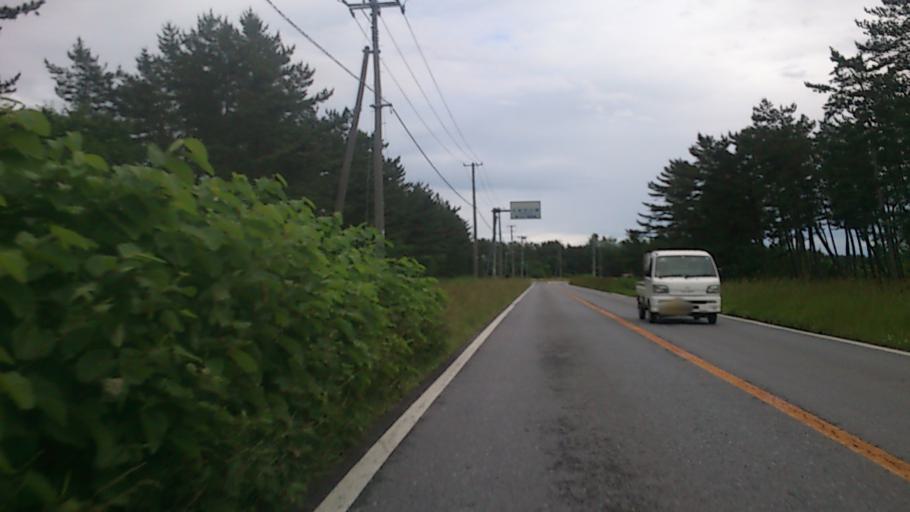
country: JP
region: Akita
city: Tenno
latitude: 40.0145
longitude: 139.9530
